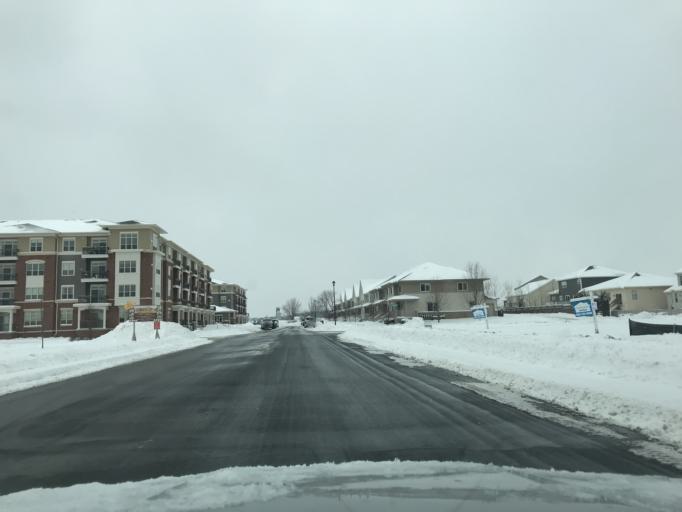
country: US
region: Wisconsin
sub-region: Dane County
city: Sun Prairie
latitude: 43.1717
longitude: -89.2720
